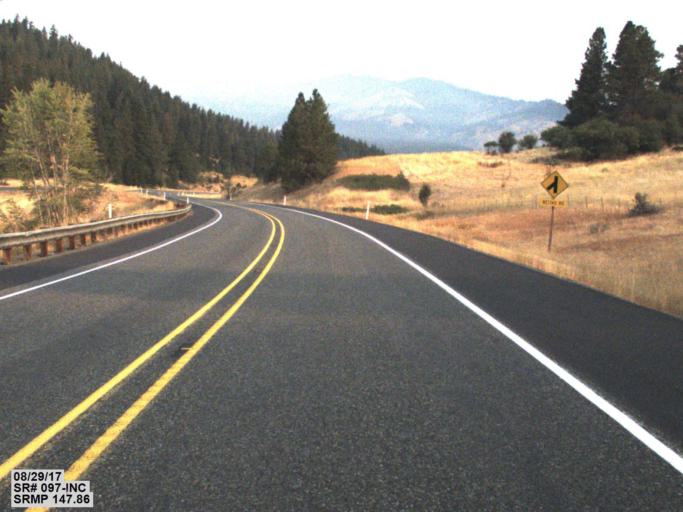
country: US
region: Washington
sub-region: Kittitas County
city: Cle Elum
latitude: 47.1773
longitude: -120.7028
